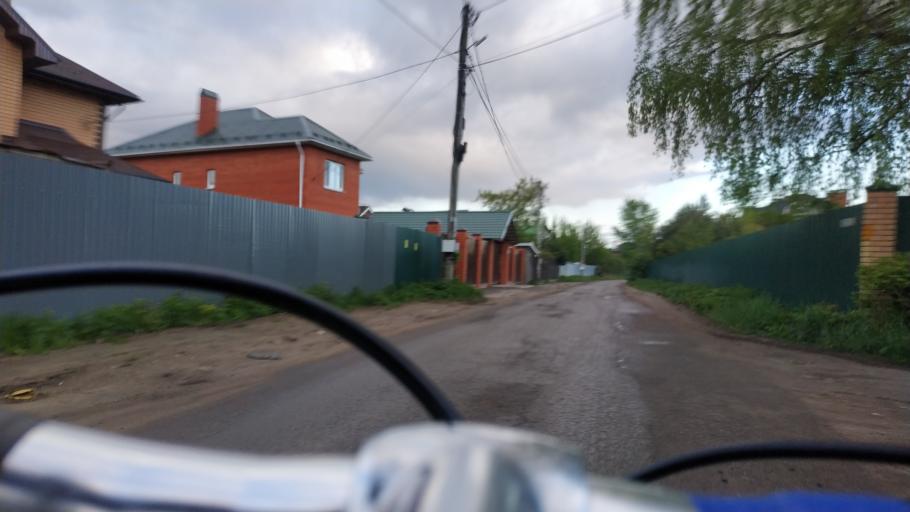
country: RU
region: Moskovskaya
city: Ramenskoye
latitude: 55.5796
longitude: 38.3013
